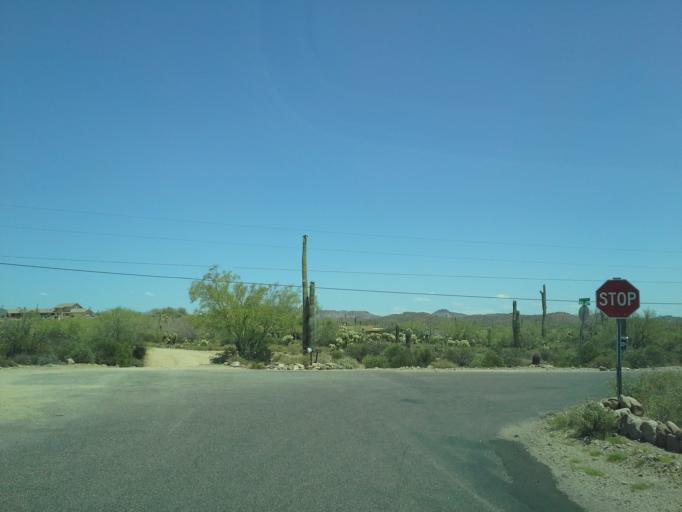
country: US
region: Arizona
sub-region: Pinal County
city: Apache Junction
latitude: 33.3842
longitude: -111.4297
